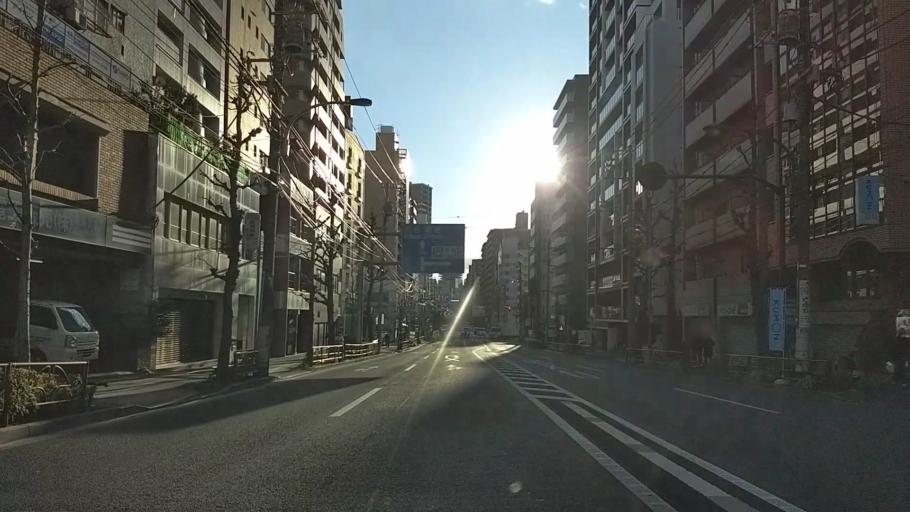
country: JP
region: Tokyo
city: Tokyo
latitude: 35.7416
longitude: 139.7257
